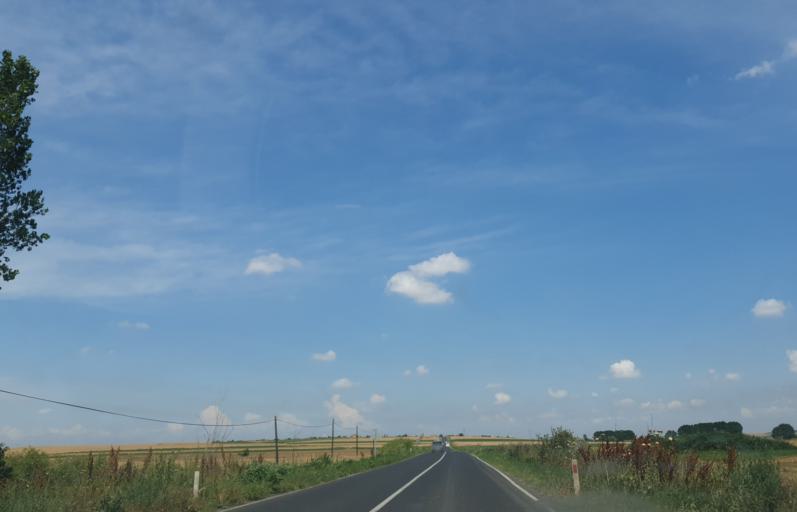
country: TR
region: Kirklareli
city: Buyukkaristiran
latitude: 41.2265
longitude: 27.5591
